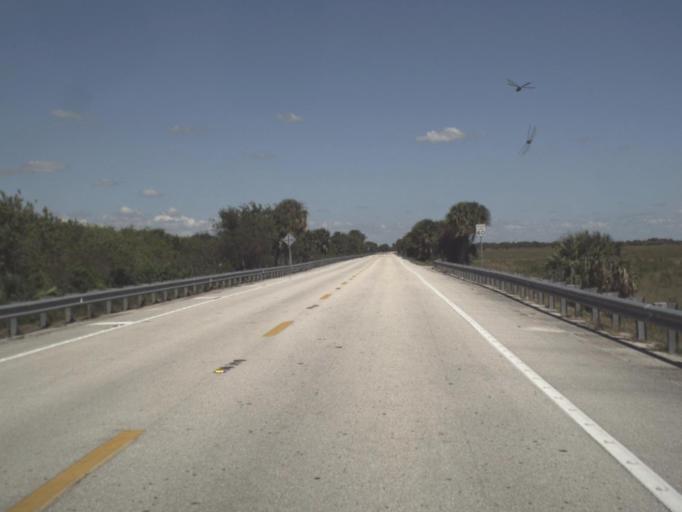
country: US
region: Florida
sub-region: Glades County
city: Buckhead Ridge
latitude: 27.0696
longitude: -80.9767
